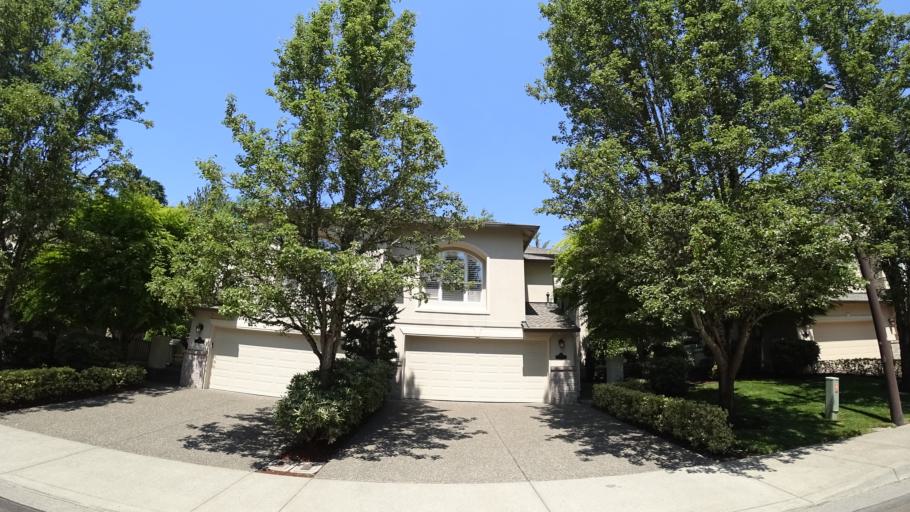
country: US
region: Oregon
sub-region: Washington County
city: Durham
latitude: 45.4265
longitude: -122.7271
